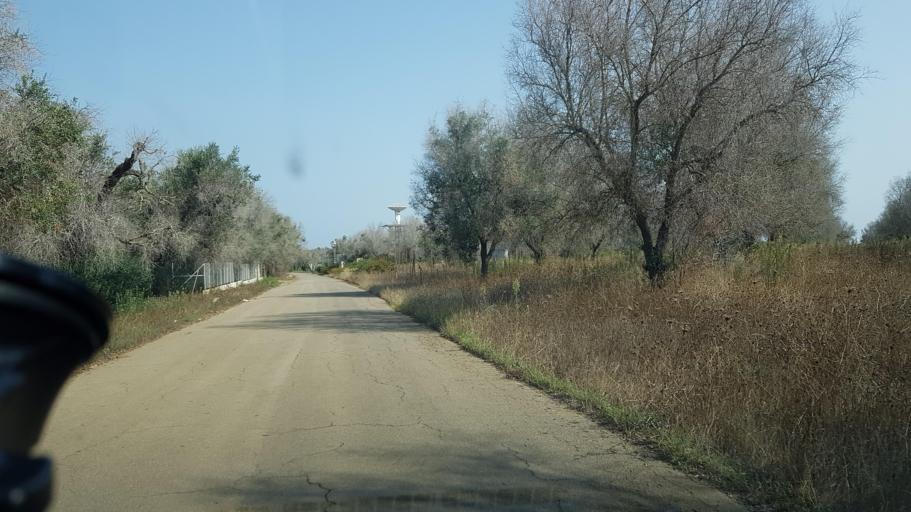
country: IT
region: Apulia
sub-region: Provincia di Brindisi
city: Torchiarolo
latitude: 40.5051
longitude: 18.0590
